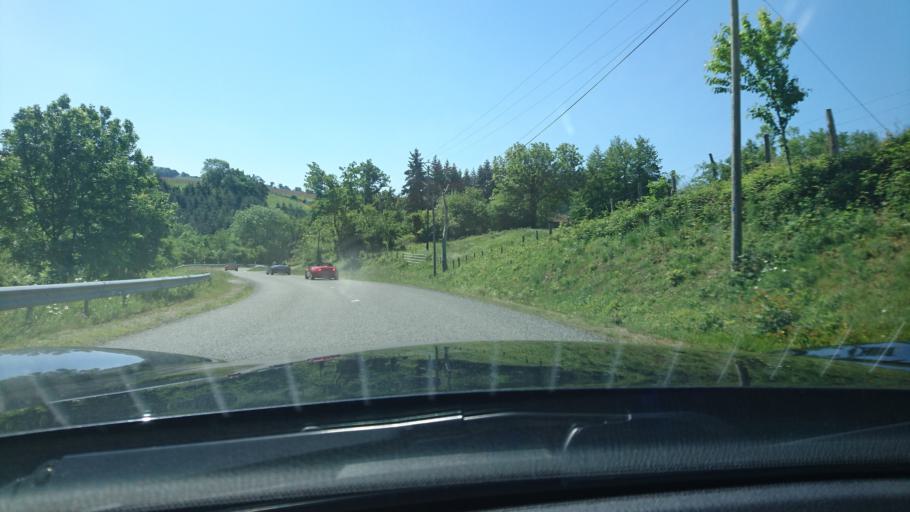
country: FR
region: Rhone-Alpes
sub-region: Departement de la Loire
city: Saint-Just-la-Pendue
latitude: 45.8895
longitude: 4.3022
